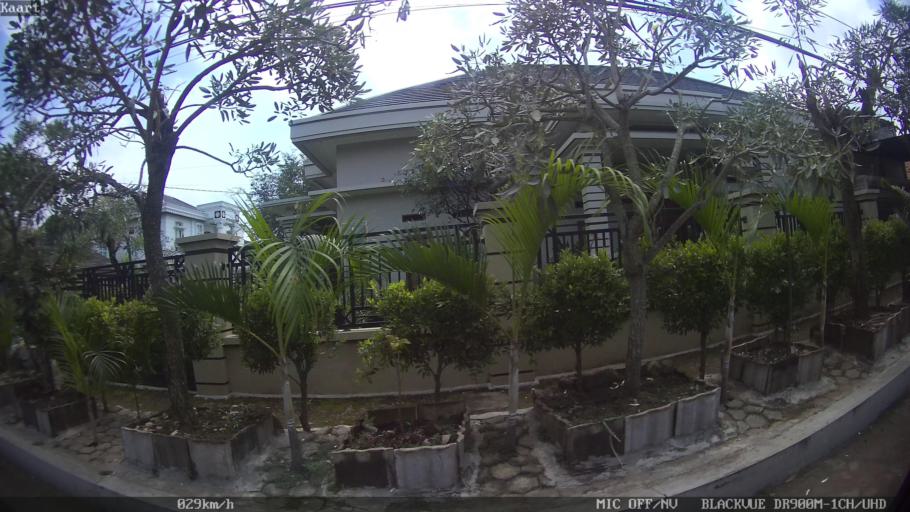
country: ID
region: Lampung
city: Kedaton
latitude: -5.3661
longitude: 105.3025
